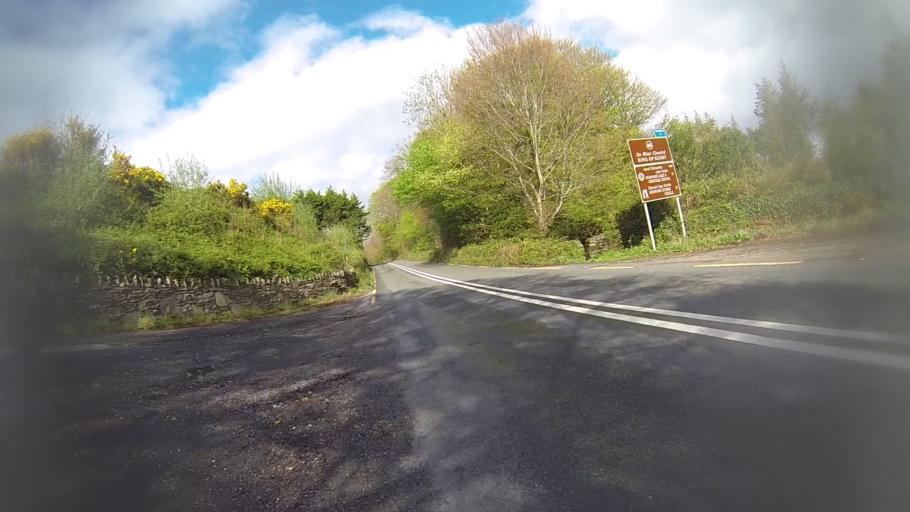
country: IE
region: Munster
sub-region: Ciarrai
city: Kenmare
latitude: 51.8539
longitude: -9.7335
